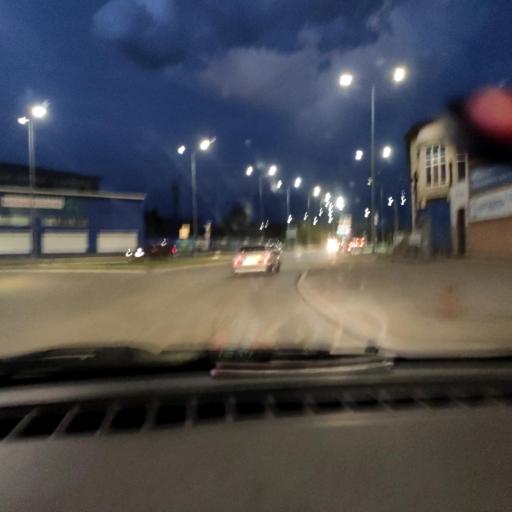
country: RU
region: Orenburg
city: Orenburg
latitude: 51.8042
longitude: 55.1587
